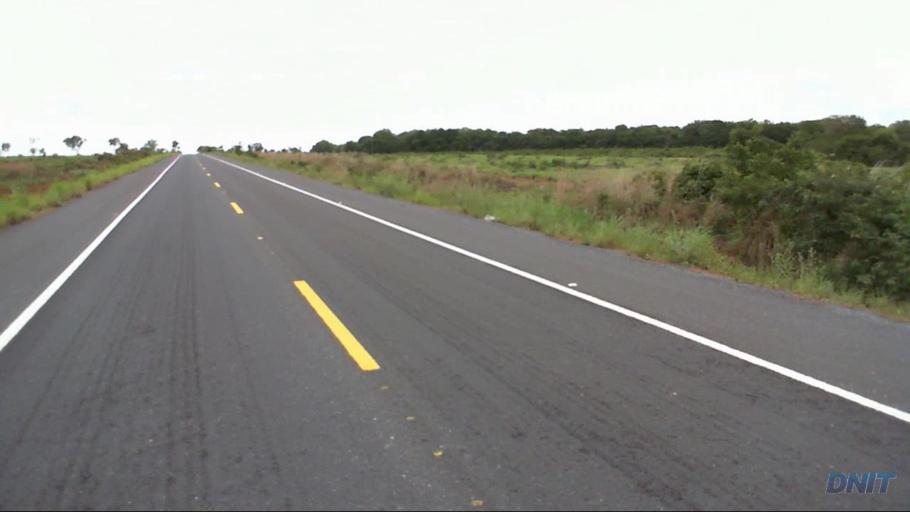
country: BR
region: Goias
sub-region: Sao Miguel Do Araguaia
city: Sao Miguel do Araguaia
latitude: -13.2893
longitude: -50.4369
